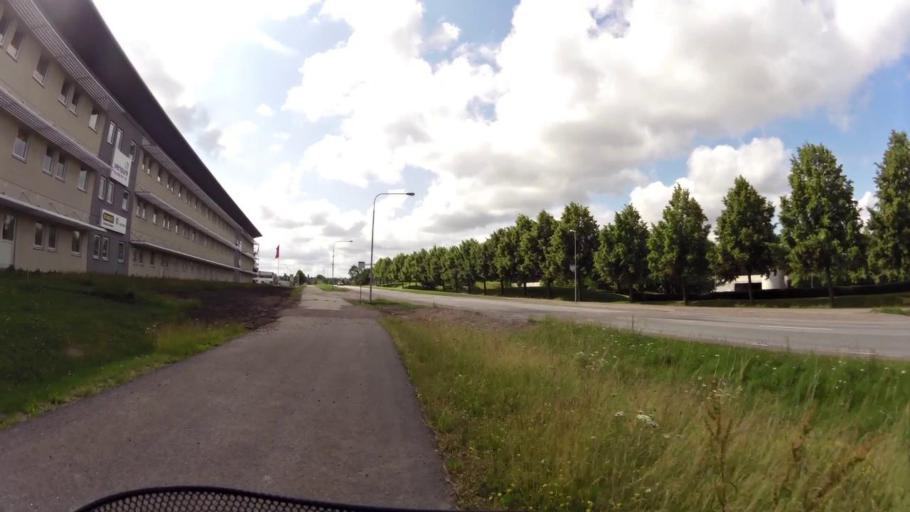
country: SE
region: OEstergoetland
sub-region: Linkopings Kommun
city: Linkoping
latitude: 58.4209
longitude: 15.6364
